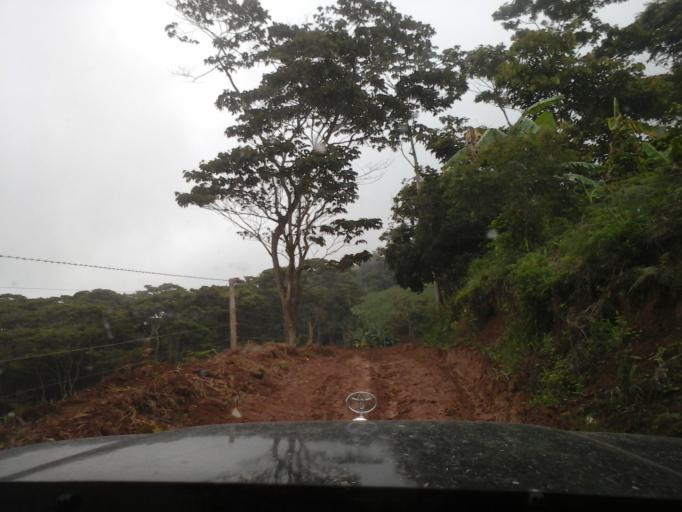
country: CO
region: Cesar
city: Agustin Codazzi
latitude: 9.9605
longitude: -73.0621
